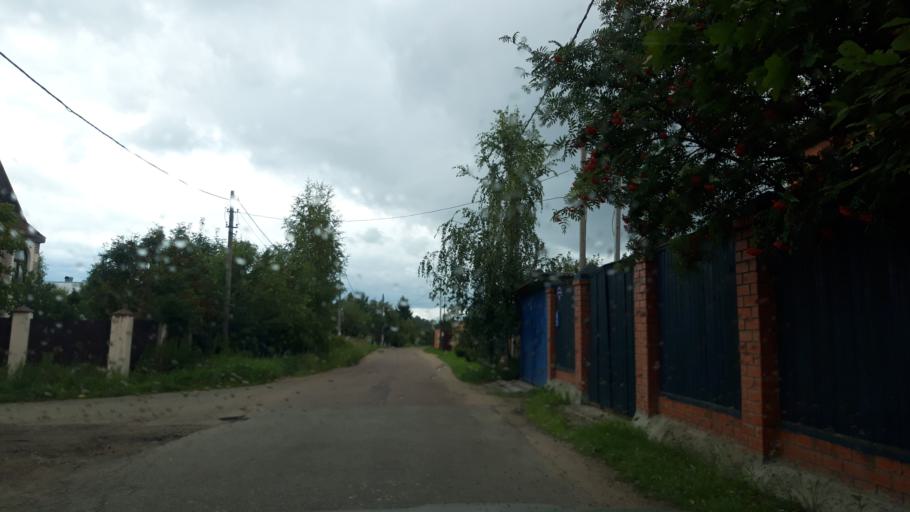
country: RU
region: Moskovskaya
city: Povarovo
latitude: 56.0947
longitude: 37.0721
